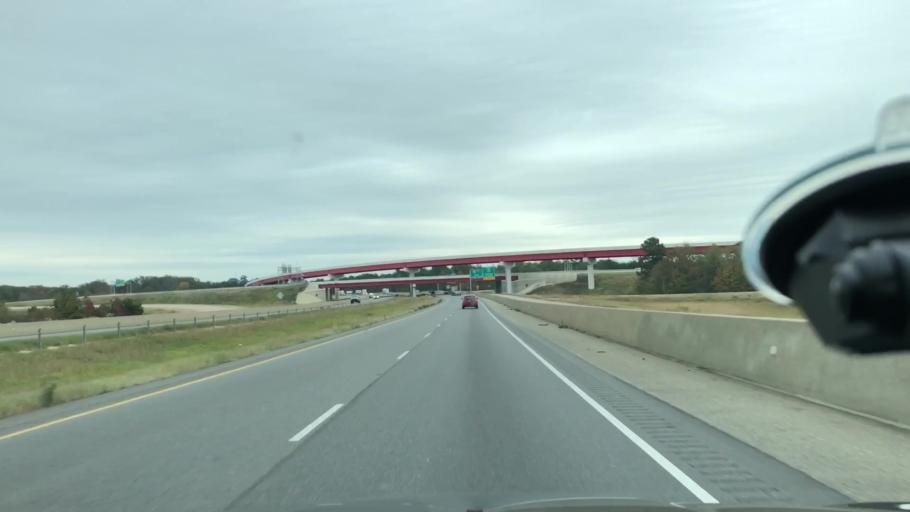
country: US
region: Arkansas
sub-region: Miller County
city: Texarkana
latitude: 33.4789
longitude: -93.9907
